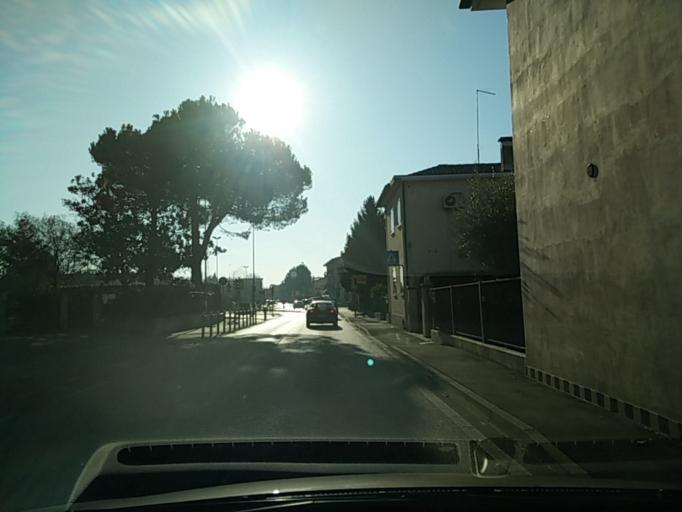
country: IT
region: Veneto
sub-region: Provincia di Treviso
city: Silea
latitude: 45.6625
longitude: 12.2917
